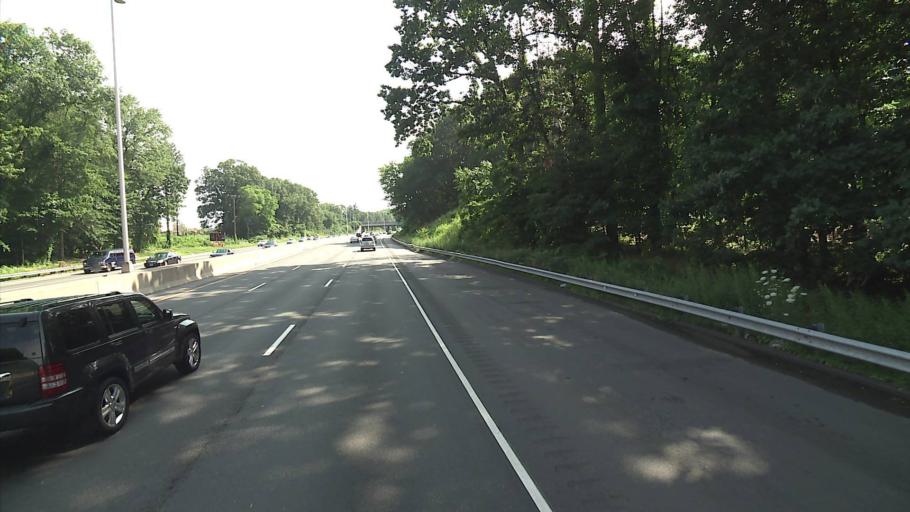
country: US
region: Connecticut
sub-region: Fairfield County
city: Darien
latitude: 41.0967
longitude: -73.4428
